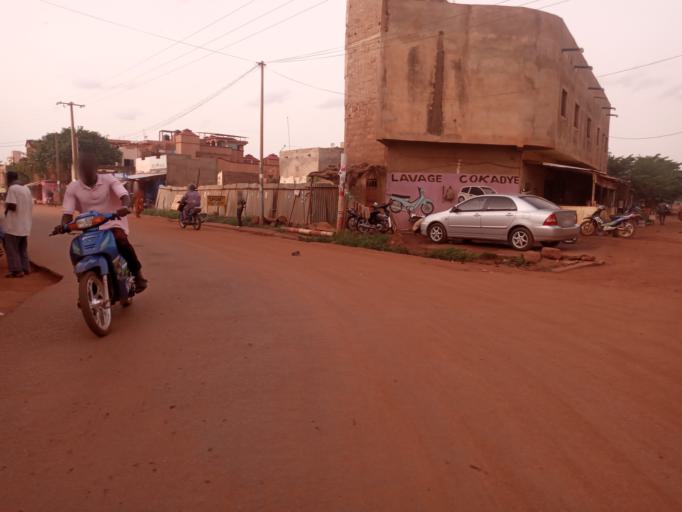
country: ML
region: Bamako
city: Bamako
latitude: 12.5543
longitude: -7.9905
